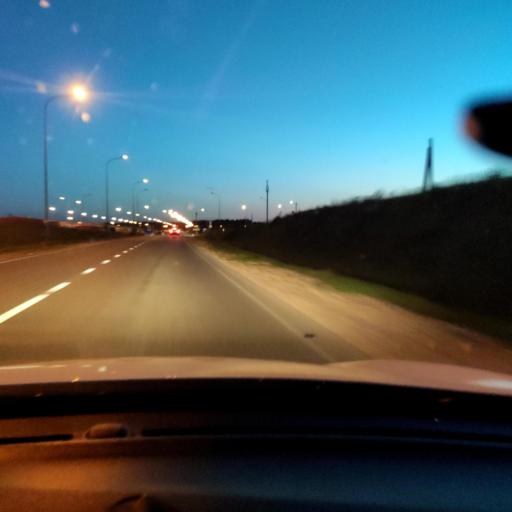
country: RU
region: Tatarstan
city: Osinovo
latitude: 55.8577
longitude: 48.8427
